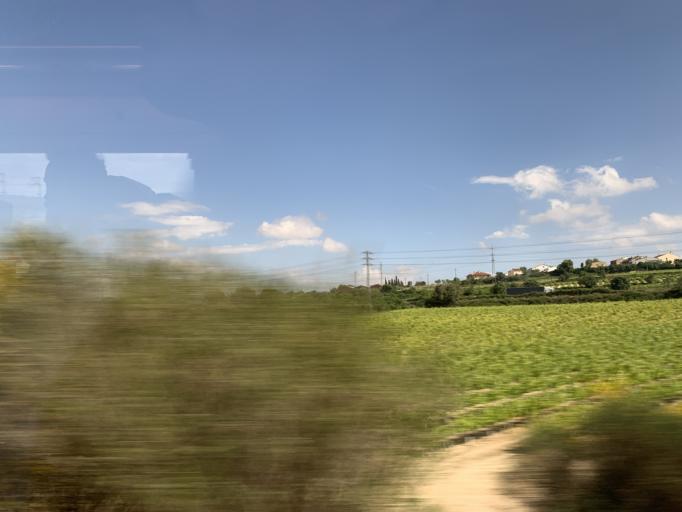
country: ES
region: Catalonia
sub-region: Provincia de Barcelona
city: Vilafranca del Penedes
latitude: 41.3312
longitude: 1.6912
